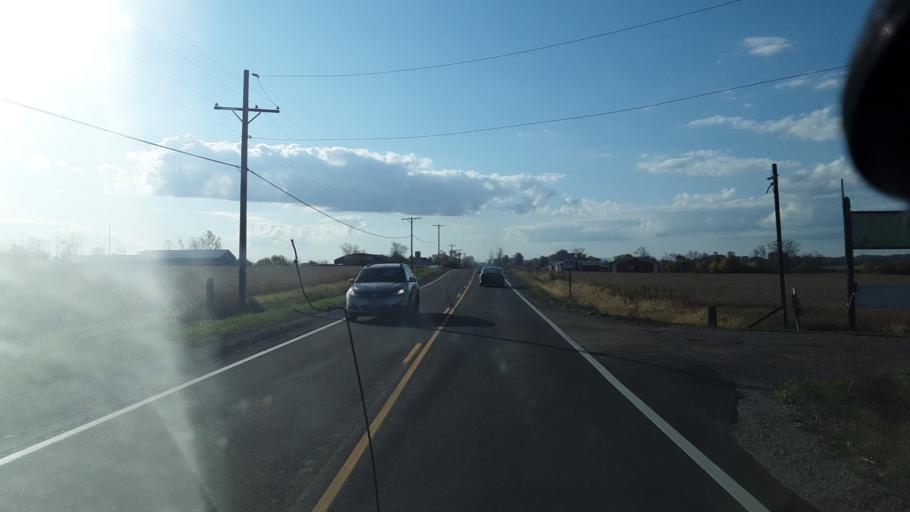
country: US
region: Ohio
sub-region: Fayette County
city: Jeffersonville
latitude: 39.6434
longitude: -83.5357
